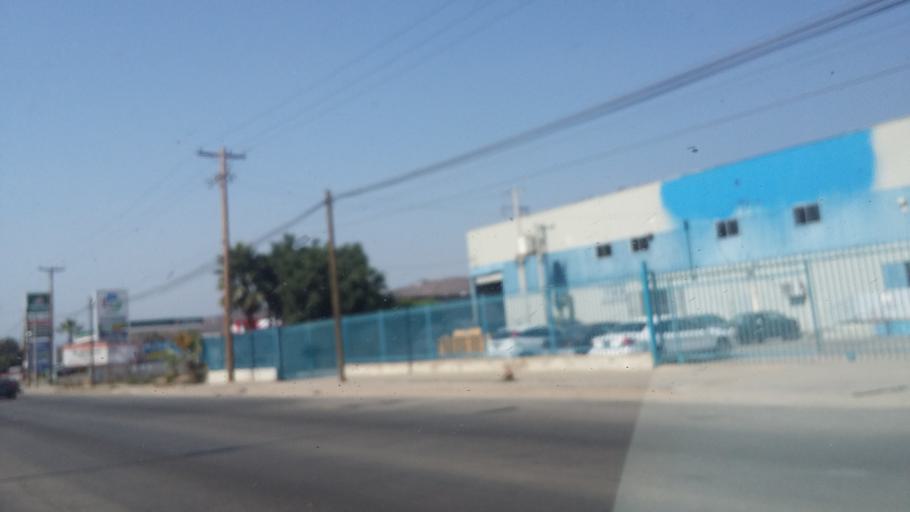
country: MX
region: Baja California
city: Ensenada
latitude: 31.8025
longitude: -116.5951
